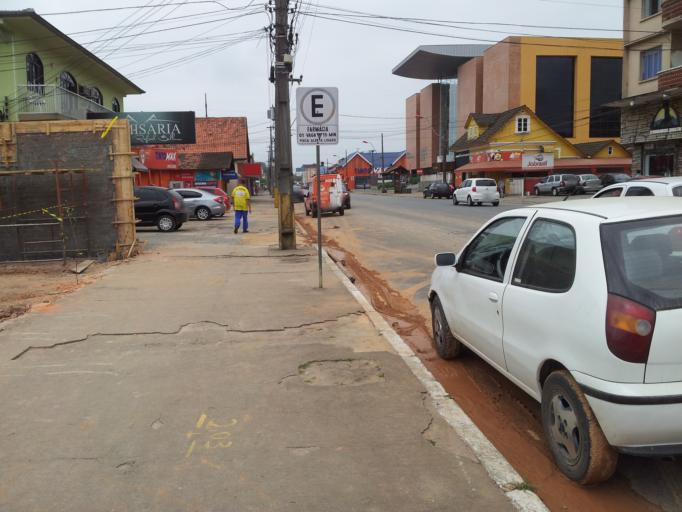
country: BR
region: Santa Catarina
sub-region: Joinville
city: Joinville
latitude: -26.3178
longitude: -48.8451
